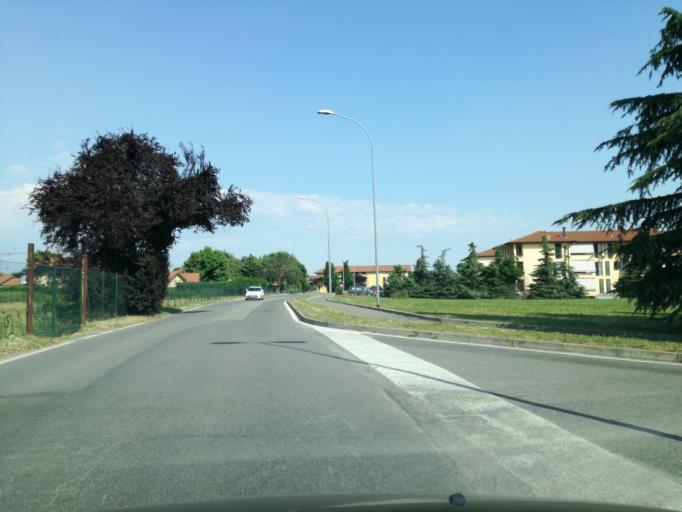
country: IT
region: Lombardy
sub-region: Provincia di Lecco
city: Cernusco Lombardone
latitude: 45.6831
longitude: 9.4088
